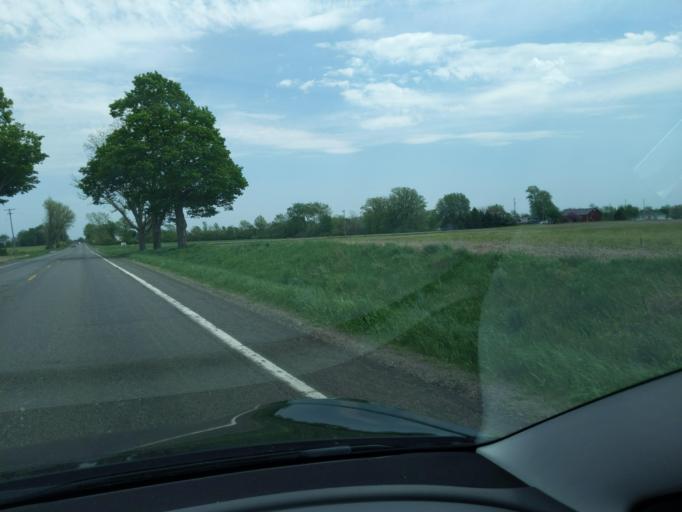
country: US
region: Michigan
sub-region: Ingham County
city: Mason
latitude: 42.5241
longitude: -84.4646
